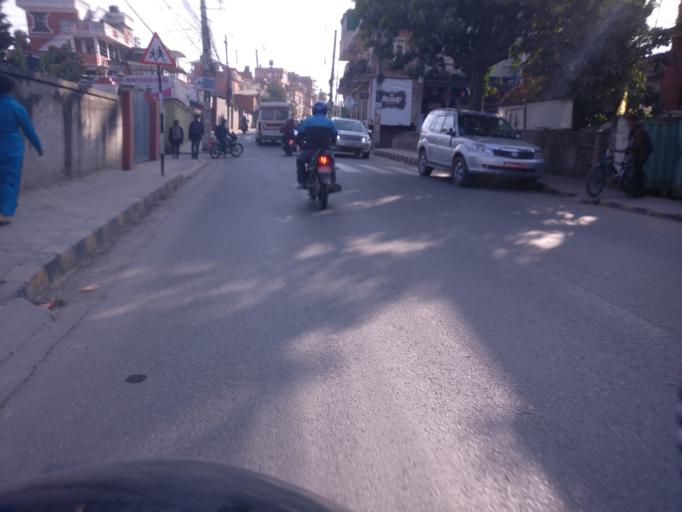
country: NP
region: Central Region
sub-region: Bagmati Zone
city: Patan
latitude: 27.6841
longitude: 85.3070
